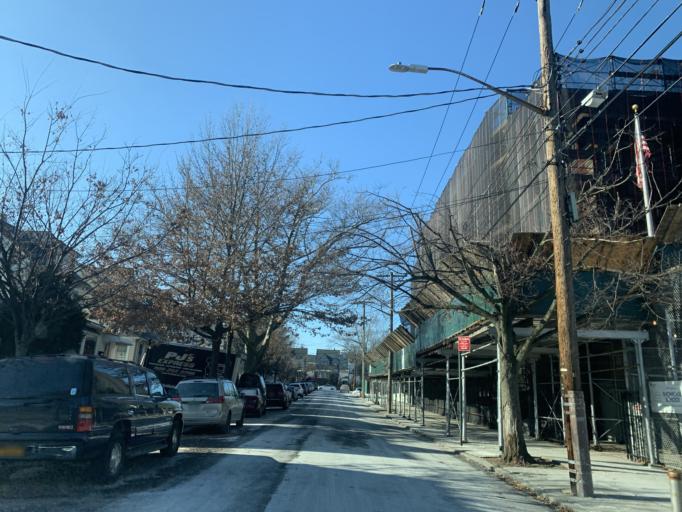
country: US
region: New York
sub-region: Nassau County
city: East Atlantic Beach
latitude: 40.7858
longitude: -73.8168
